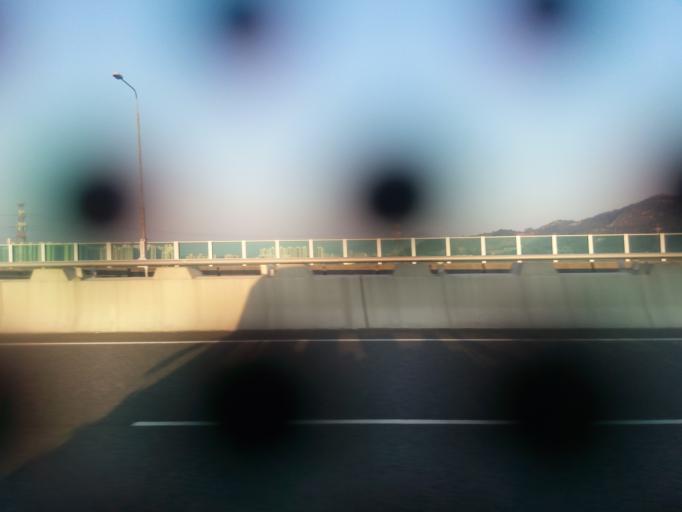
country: HK
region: Tuen Mun
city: Tuen Mun
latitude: 22.4229
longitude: 113.9845
